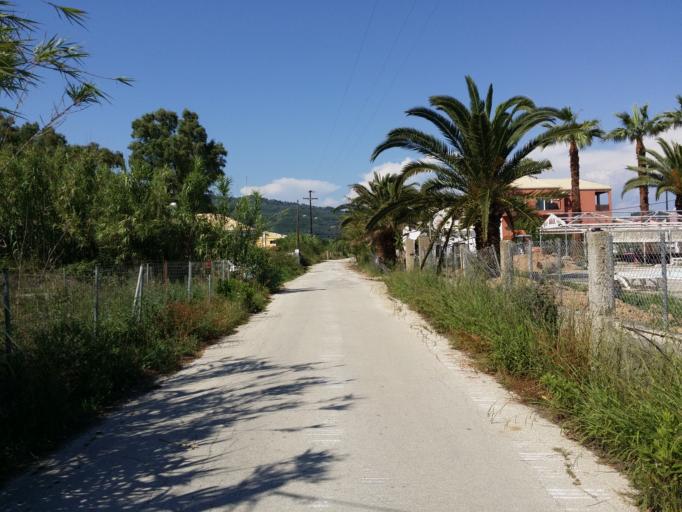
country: GR
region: Ionian Islands
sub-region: Nomos Kerkyras
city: Perivoli
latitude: 39.4288
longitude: 19.9431
